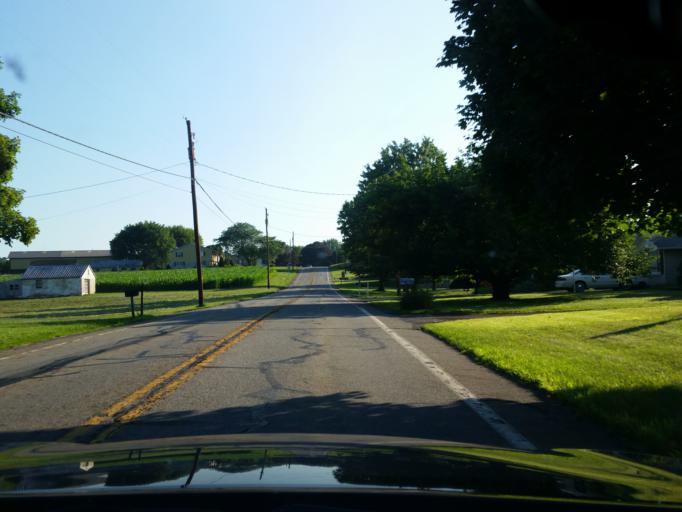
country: US
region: Pennsylvania
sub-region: Dauphin County
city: Matamoras
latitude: 40.4301
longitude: -76.9359
